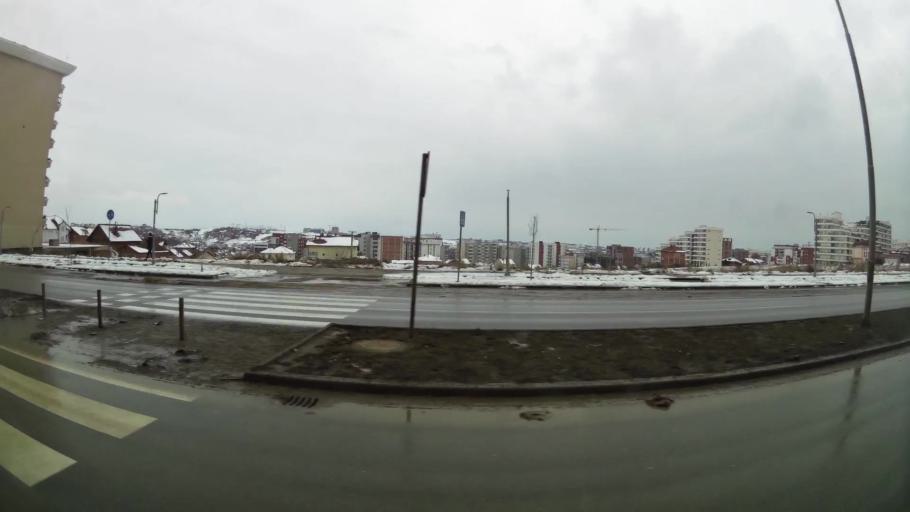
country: XK
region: Pristina
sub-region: Komuna e Prishtines
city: Pristina
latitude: 42.6498
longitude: 21.1796
